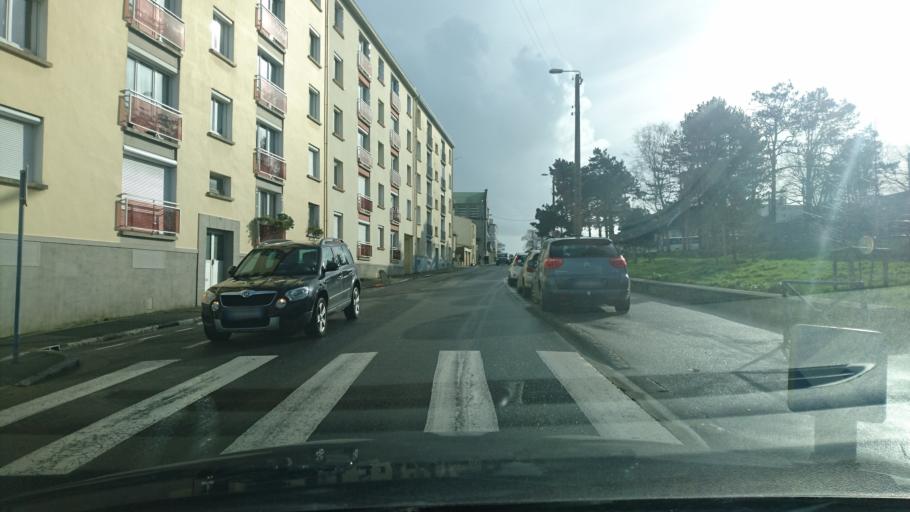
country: FR
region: Brittany
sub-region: Departement du Finistere
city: Brest
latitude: 48.3888
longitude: -4.5035
